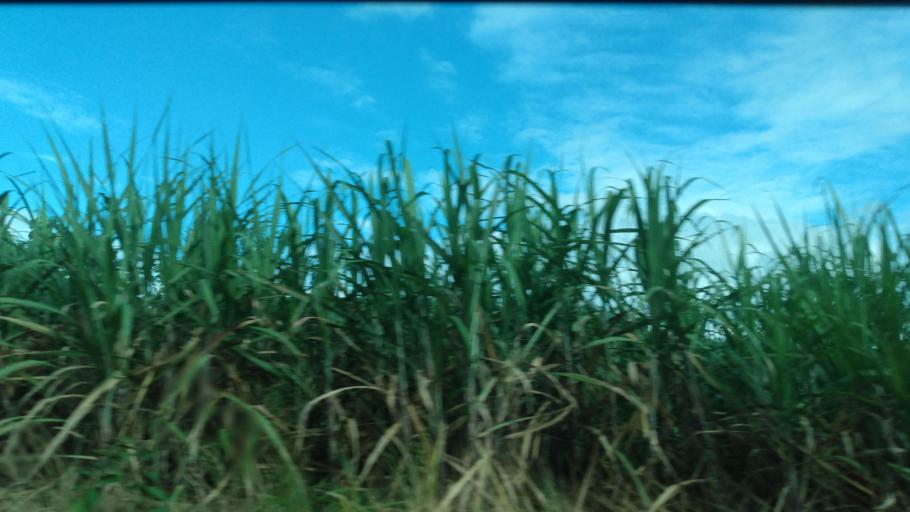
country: BR
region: Pernambuco
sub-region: Palmares
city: Palmares
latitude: -8.6926
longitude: -35.6401
